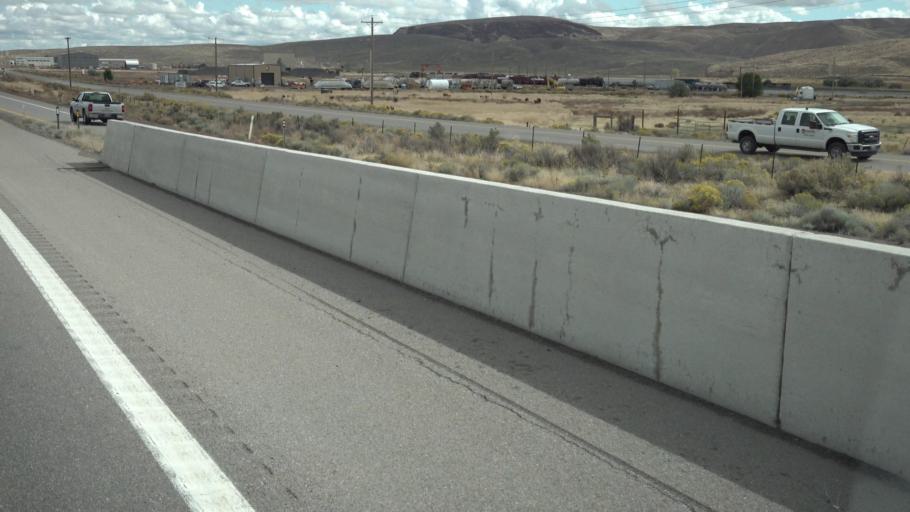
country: US
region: Nevada
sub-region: Elko County
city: Elko
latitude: 40.9349
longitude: -115.6632
